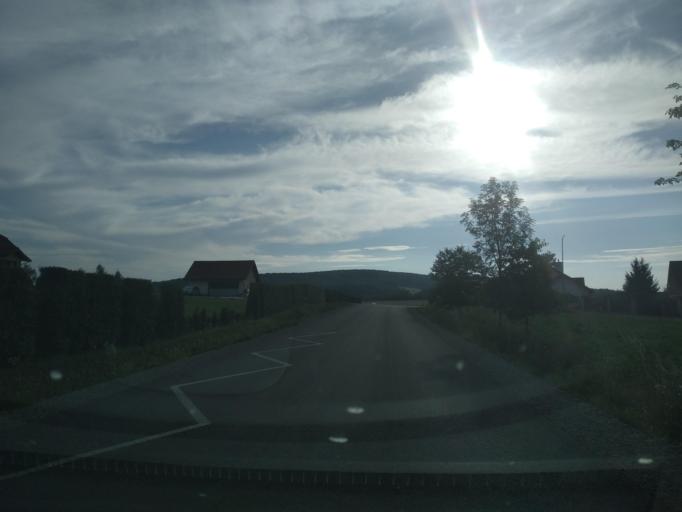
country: PL
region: Subcarpathian Voivodeship
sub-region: Powiat sanocki
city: Strachocina
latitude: 49.5734
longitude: 22.1369
